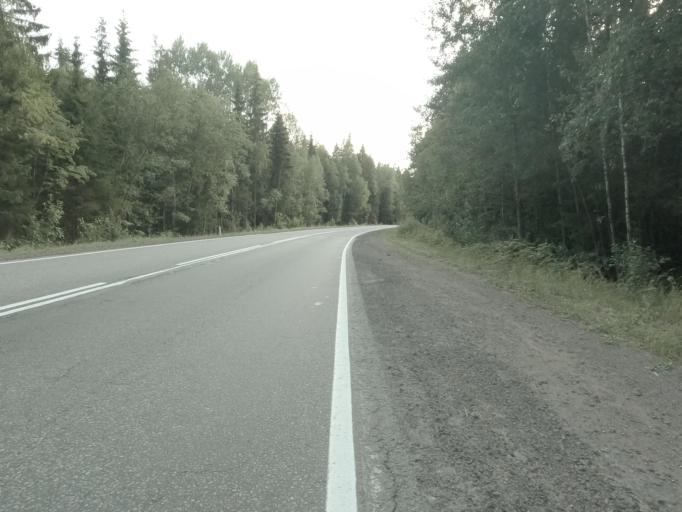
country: RU
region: Leningrad
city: Vyborg
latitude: 60.8434
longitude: 28.8514
